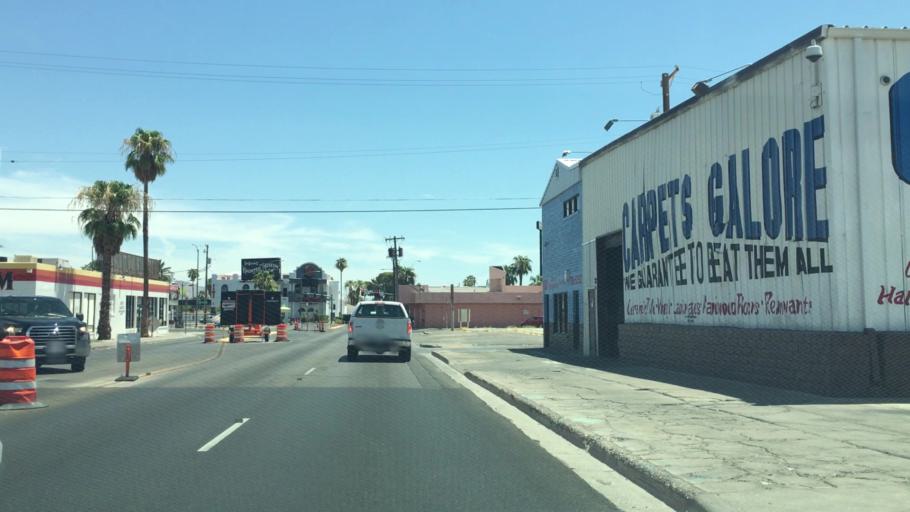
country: US
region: Nevada
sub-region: Clark County
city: Las Vegas
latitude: 36.1521
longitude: -115.1539
